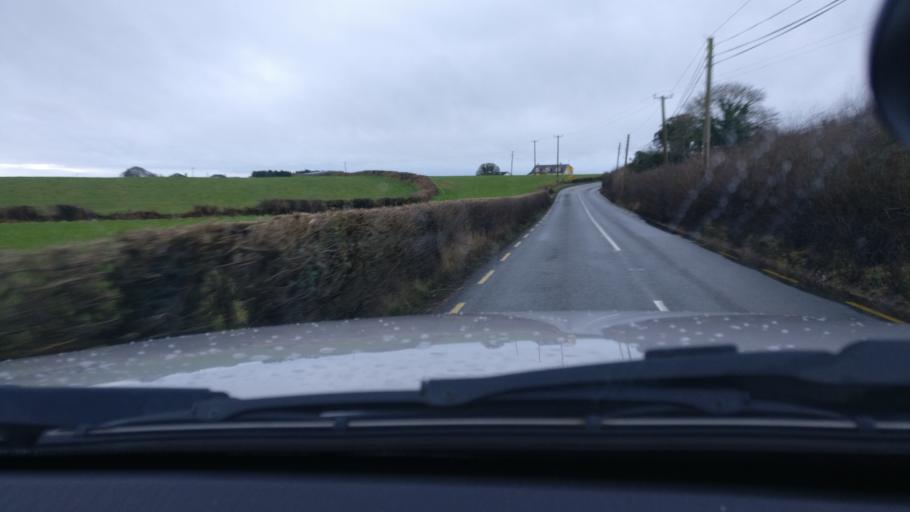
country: IE
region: Leinster
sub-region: An Longfort
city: Granard
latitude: 53.7941
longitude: -7.3936
